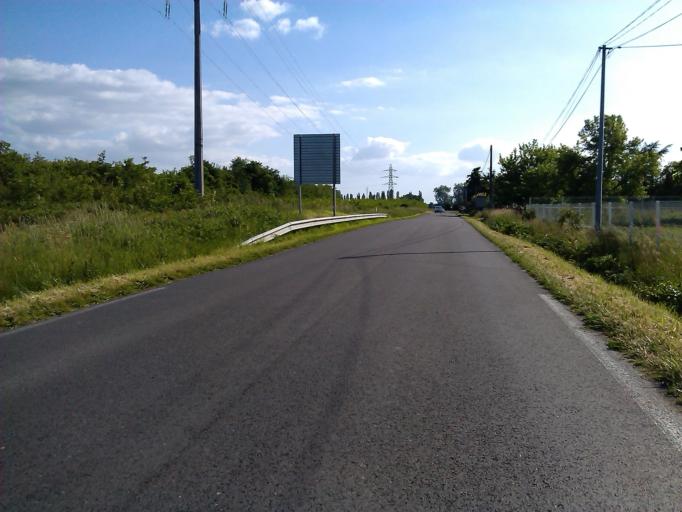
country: FR
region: Aquitaine
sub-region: Departement de la Gironde
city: Saint-Gervais
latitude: 45.0141
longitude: -0.4450
